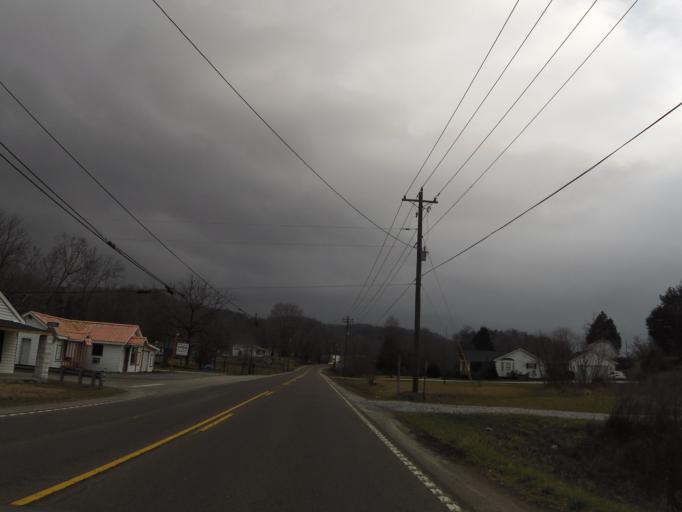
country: US
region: Tennessee
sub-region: Anderson County
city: Rocky Top
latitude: 36.2048
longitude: -84.1456
